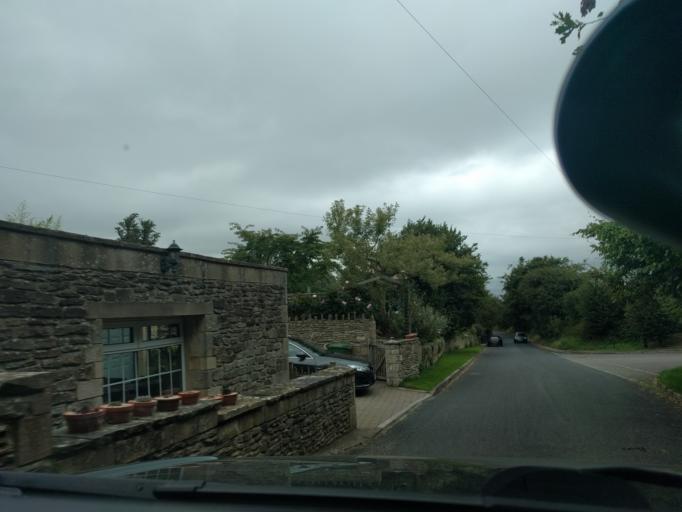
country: GB
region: England
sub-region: Wiltshire
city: Corsham
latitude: 51.4160
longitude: -2.1784
